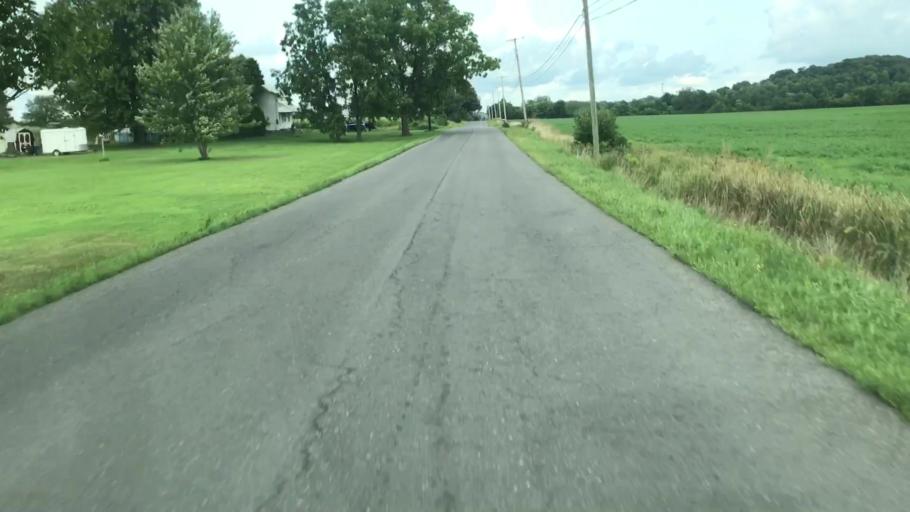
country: US
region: New York
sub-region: Onondaga County
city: Elbridge
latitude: 42.9854
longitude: -76.4934
